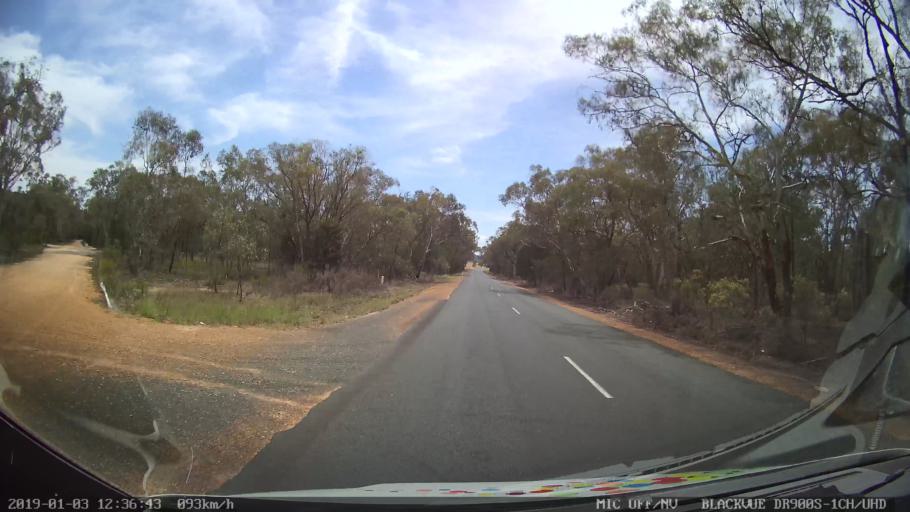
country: AU
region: New South Wales
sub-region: Weddin
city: Grenfell
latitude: -33.8513
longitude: 148.1783
